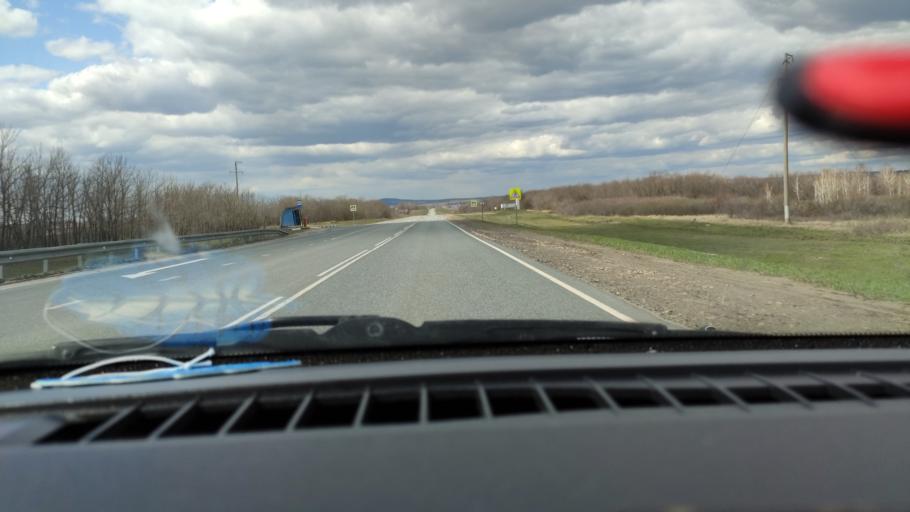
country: RU
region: Saratov
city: Tersa
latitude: 52.0841
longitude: 47.6499
